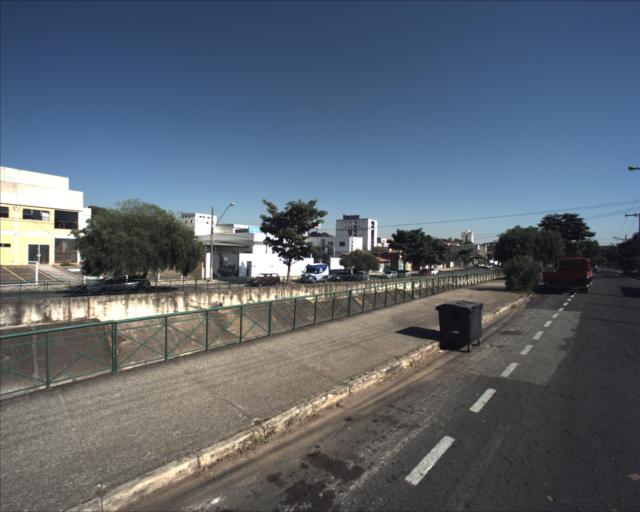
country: BR
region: Sao Paulo
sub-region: Sorocaba
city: Sorocaba
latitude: -23.5117
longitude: -47.4300
